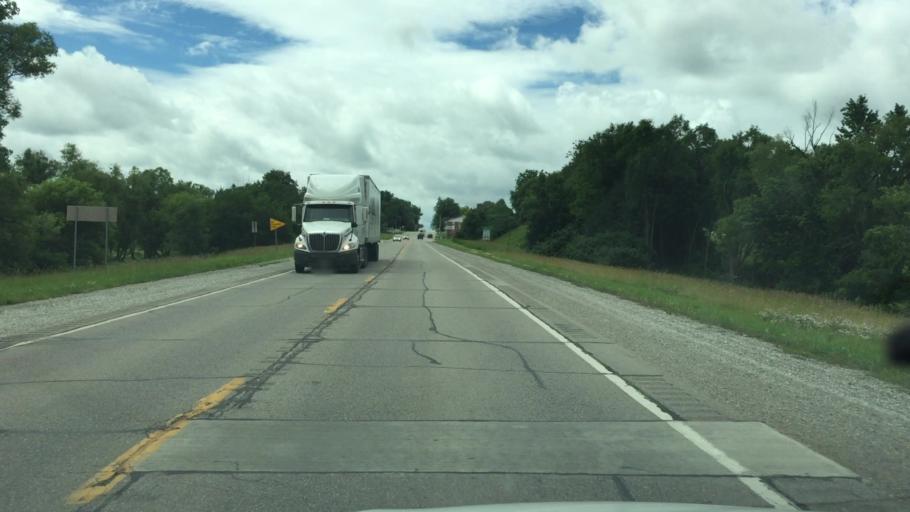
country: US
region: Iowa
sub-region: Jasper County
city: Monroe
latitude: 41.5310
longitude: -93.1020
